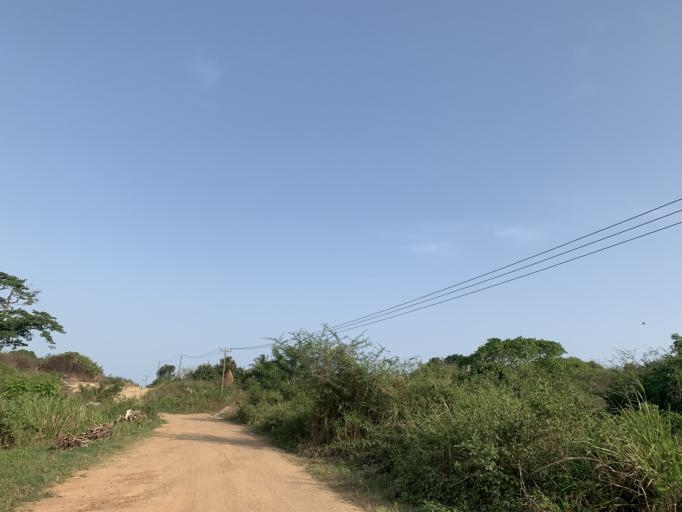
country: GH
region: Central
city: Winneba
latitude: 5.3795
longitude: -0.6175
